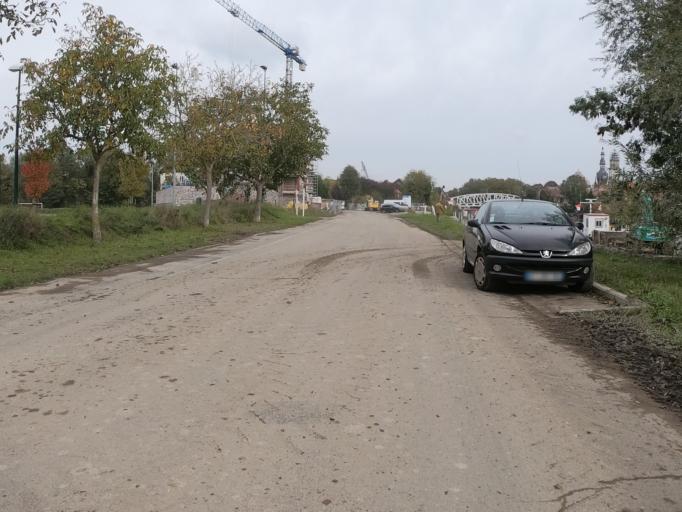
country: FR
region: Nord-Pas-de-Calais
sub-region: Departement du Nord
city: Comines
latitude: 50.7644
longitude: 3.0002
